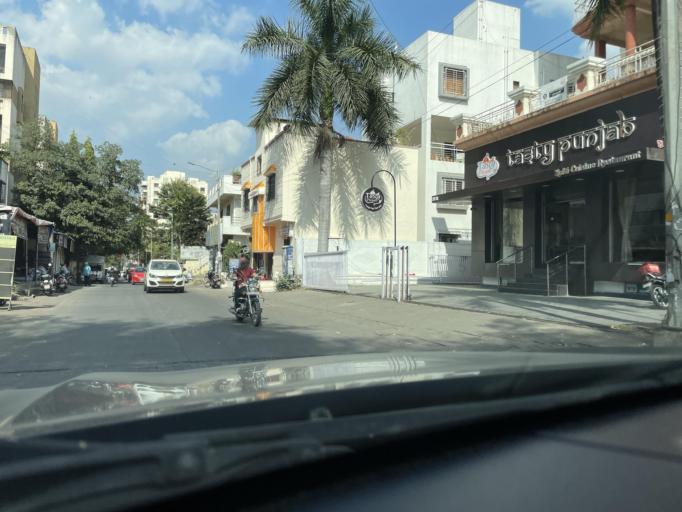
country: IN
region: Maharashtra
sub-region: Pune Division
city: Pune
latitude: 18.4818
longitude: 73.9006
